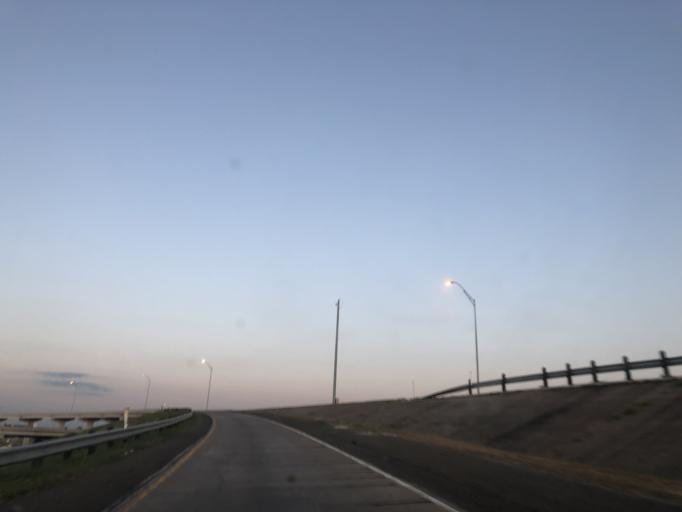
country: US
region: Texas
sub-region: Tarrant County
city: Euless
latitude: 32.8399
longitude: -97.0590
